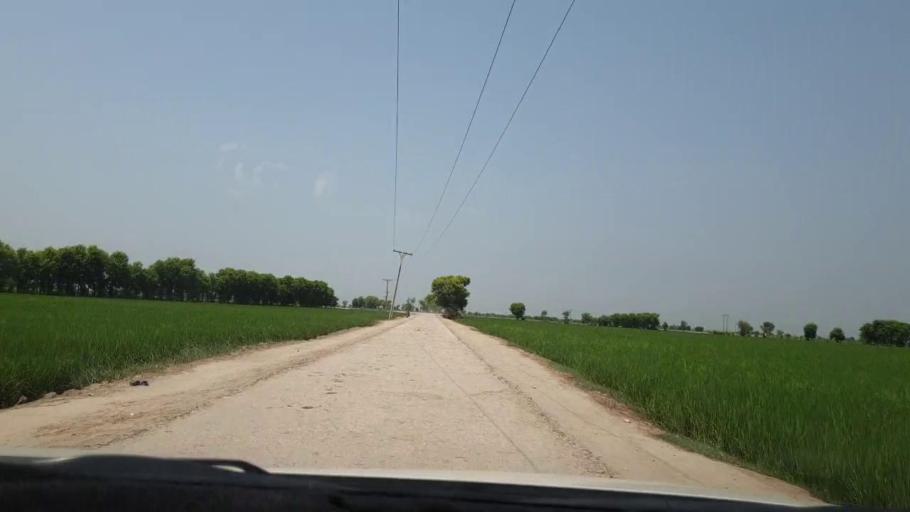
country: PK
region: Sindh
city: Radhan
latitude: 27.2484
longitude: 67.9842
